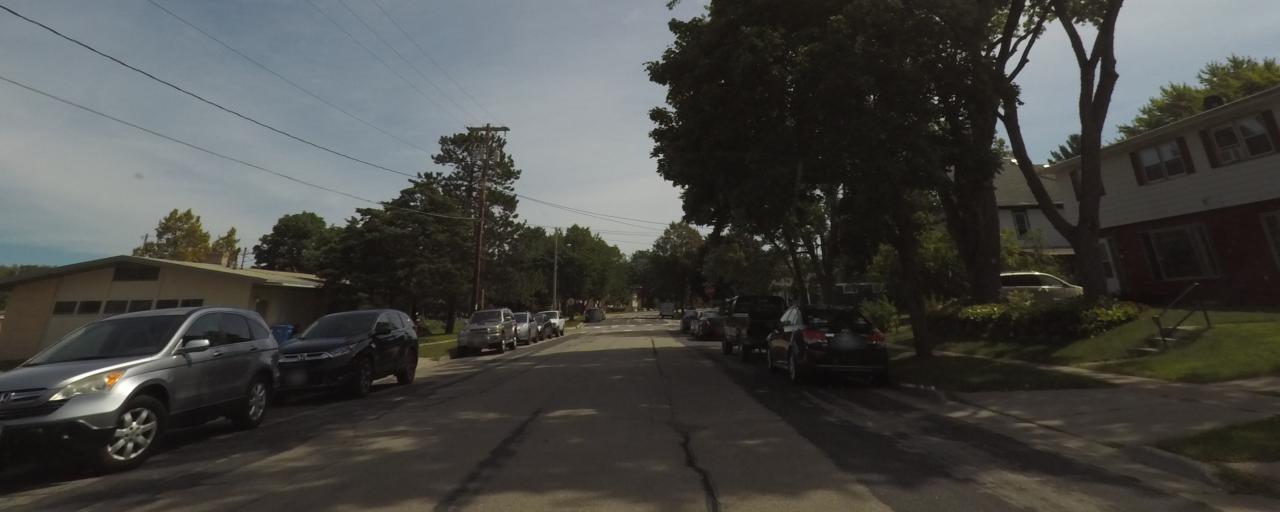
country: US
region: Wisconsin
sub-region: Dane County
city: Middleton
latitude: 43.0961
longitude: -89.4998
